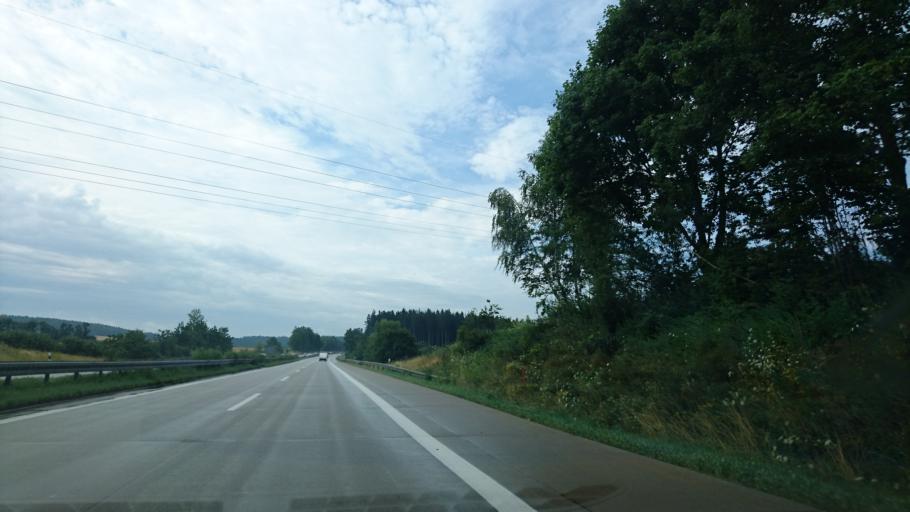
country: DE
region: Bavaria
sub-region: Lower Bavaria
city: Bad Abbach
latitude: 48.9235
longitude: 12.0882
